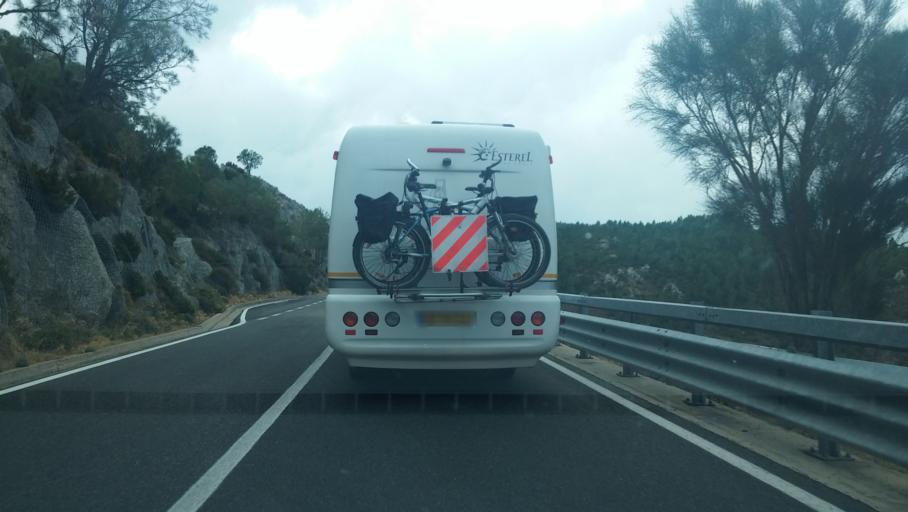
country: IT
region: Sardinia
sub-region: Provincia di Ogliastra
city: Urzulei
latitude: 40.1748
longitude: 9.5272
